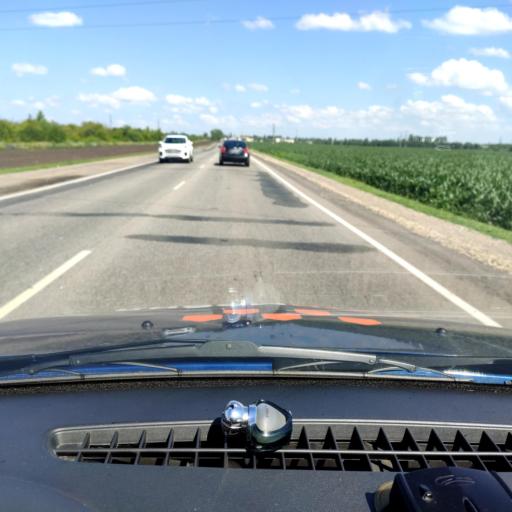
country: RU
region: Orjol
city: Livny
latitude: 52.4406
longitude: 37.5571
